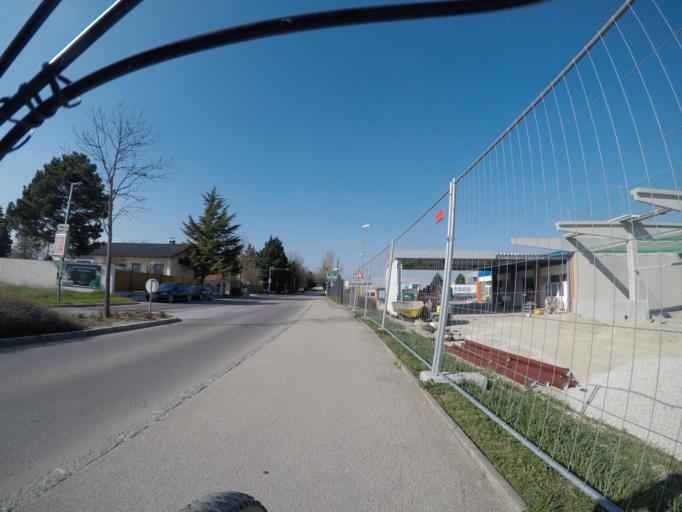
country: AT
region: Lower Austria
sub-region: Politischer Bezirk Modling
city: Neu-Guntramsdorf
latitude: 48.0582
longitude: 16.3238
